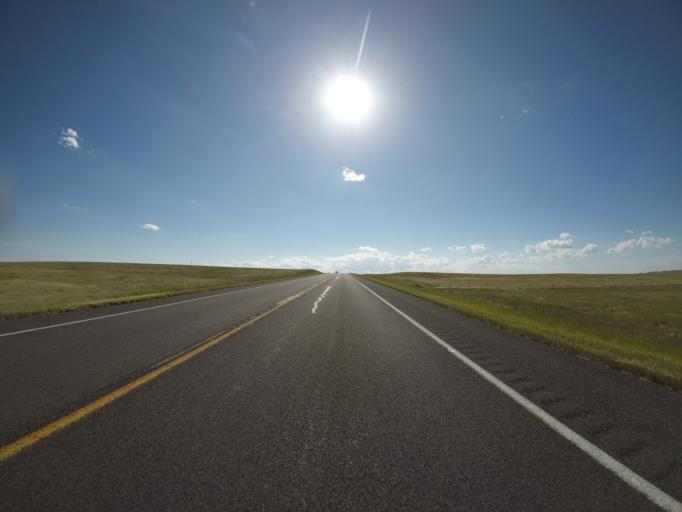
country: US
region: Colorado
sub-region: Morgan County
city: Brush
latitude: 40.6107
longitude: -103.5900
